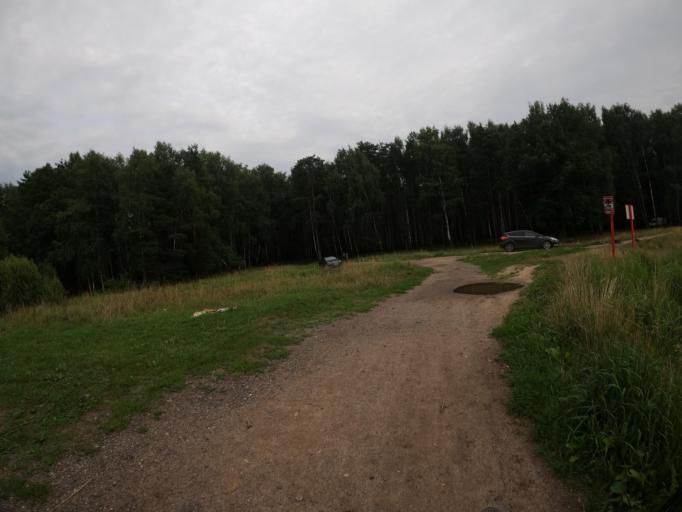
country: RU
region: Moskovskaya
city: Bykovo
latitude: 55.6519
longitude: 38.1101
